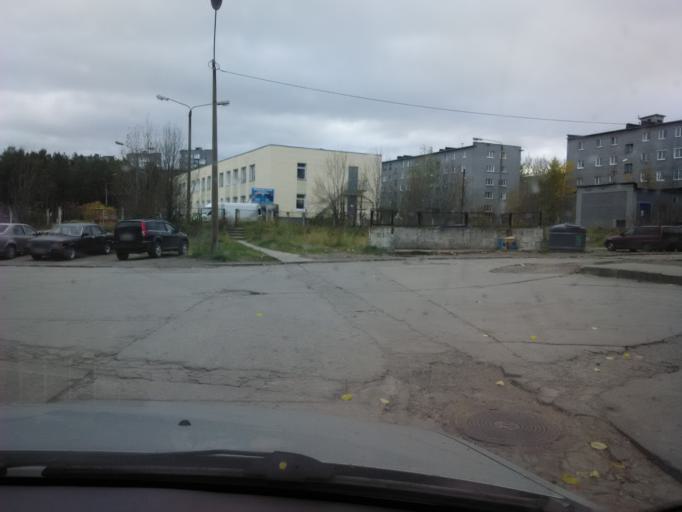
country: RU
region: Murmansk
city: Polyarnyye Zori
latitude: 67.3695
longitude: 32.5077
